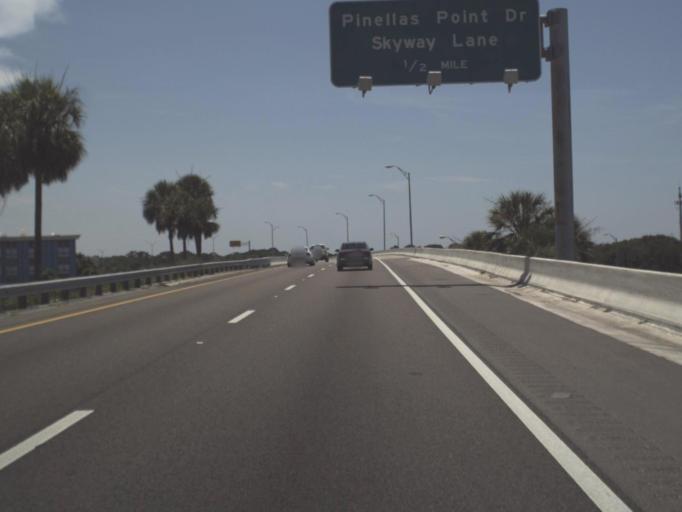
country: US
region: Florida
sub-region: Pinellas County
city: Gulfport
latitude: 27.7178
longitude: -82.6785
